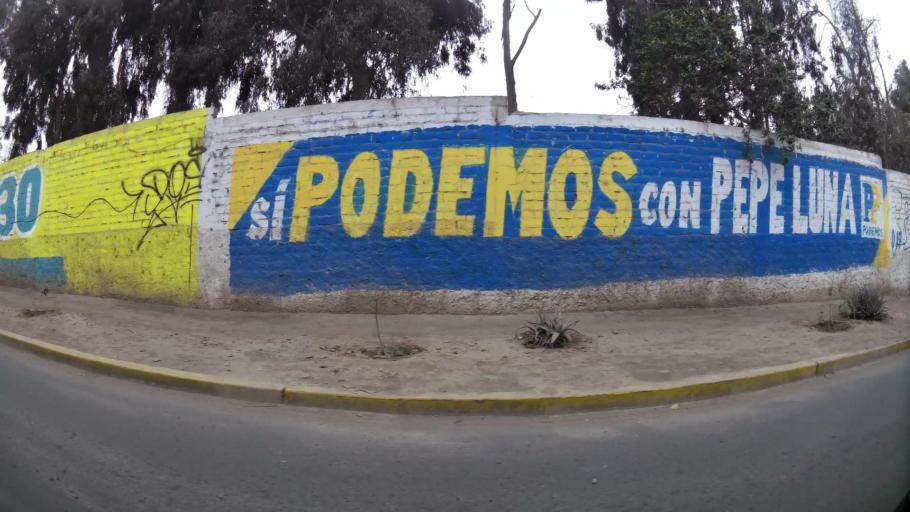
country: PE
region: Lima
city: Ventanilla
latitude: -11.9224
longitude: -77.0808
